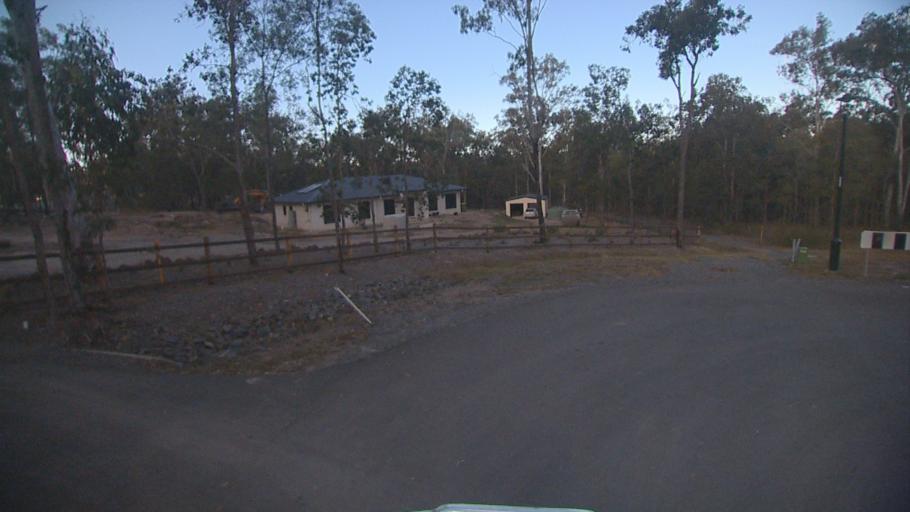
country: AU
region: Queensland
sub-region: Logan
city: Cedar Vale
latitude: -27.8594
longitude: 153.0959
